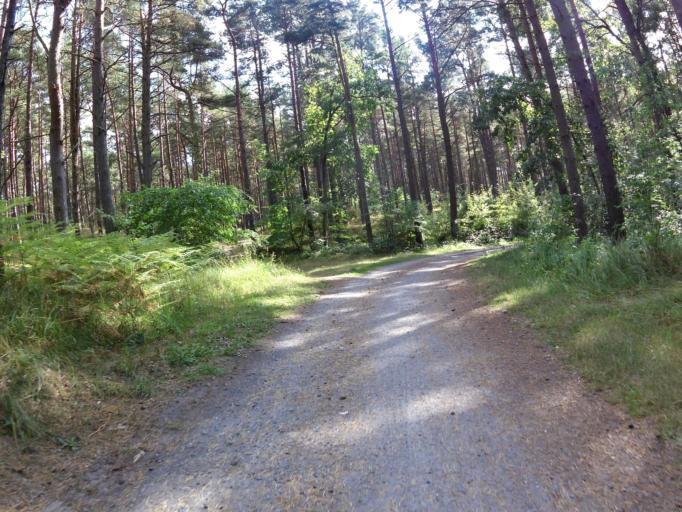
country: DE
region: Mecklenburg-Vorpommern
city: Karlshagen
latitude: 54.1107
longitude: 13.8538
